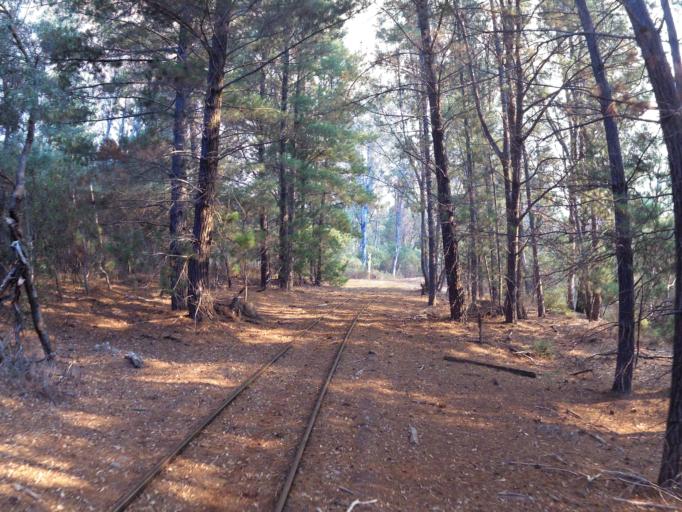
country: AU
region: Western Australia
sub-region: Waroona
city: Waroona
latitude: -32.7382
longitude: 116.1305
